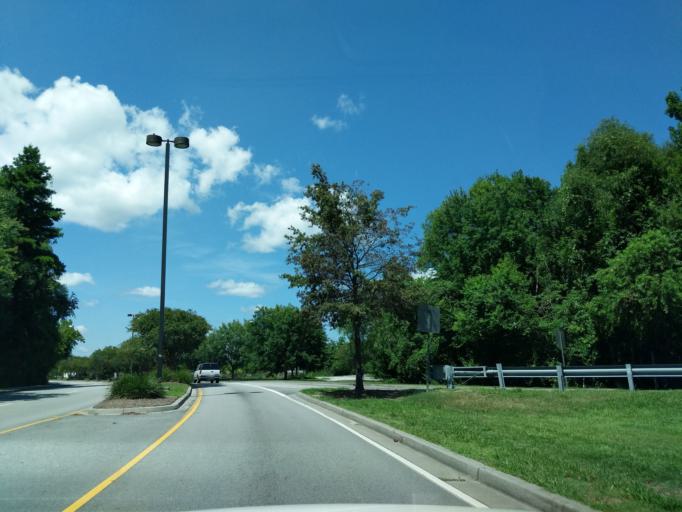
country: US
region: South Carolina
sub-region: Charleston County
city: North Charleston
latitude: 32.8702
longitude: -80.0152
